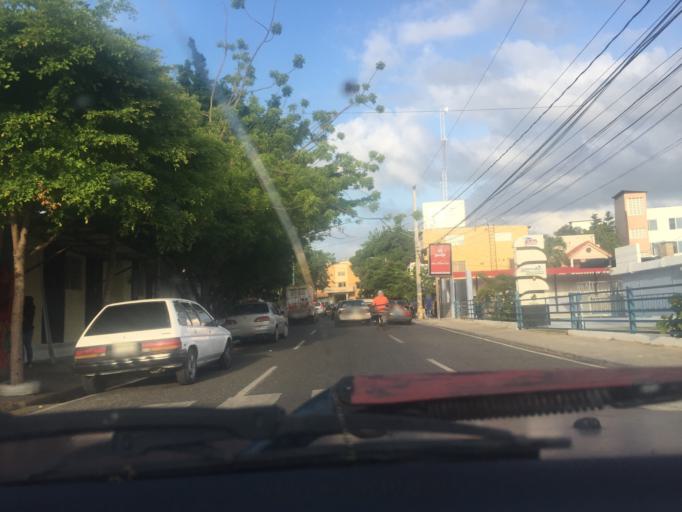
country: DO
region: Santiago
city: Santiago de los Caballeros
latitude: 19.4479
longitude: -70.6972
